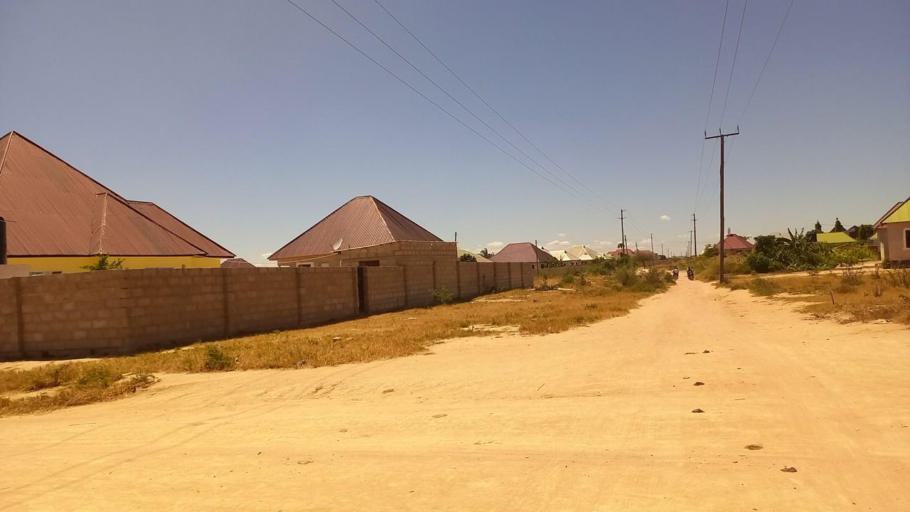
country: TZ
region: Dodoma
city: Dodoma
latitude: -6.1347
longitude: 35.7131
